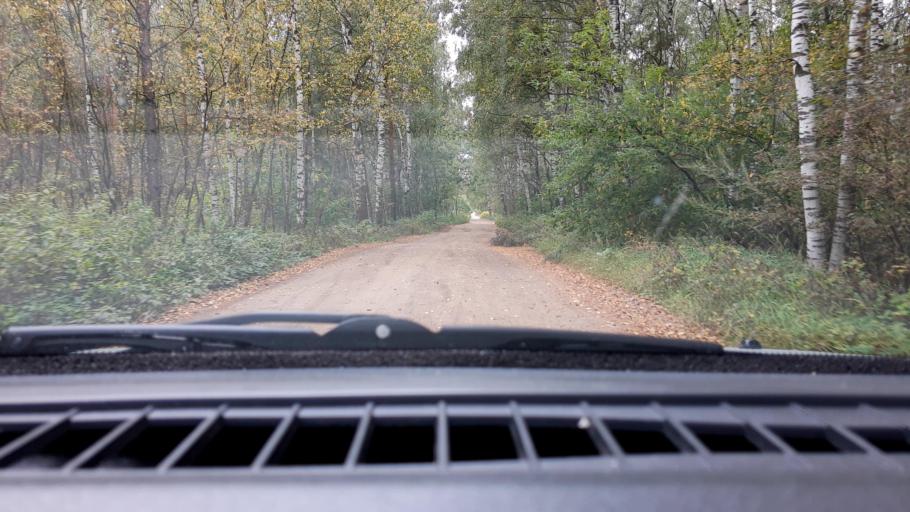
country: RU
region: Nizjnij Novgorod
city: Gorbatovka
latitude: 56.3112
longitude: 43.6977
